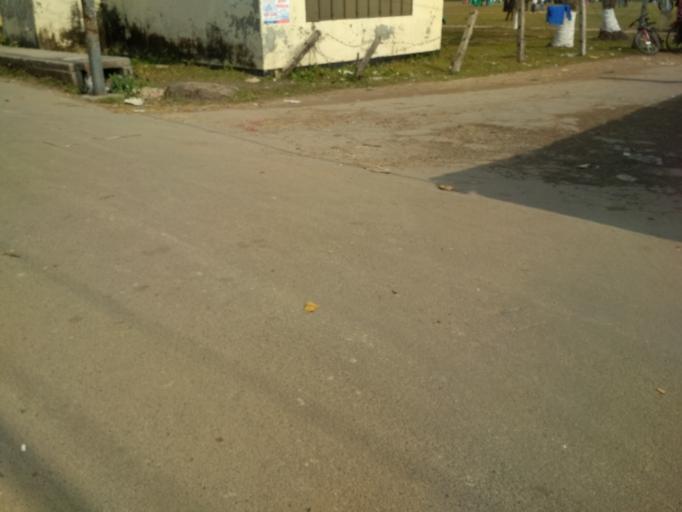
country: BD
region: Chittagong
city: Lakshmipur
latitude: 22.9323
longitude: 90.8260
